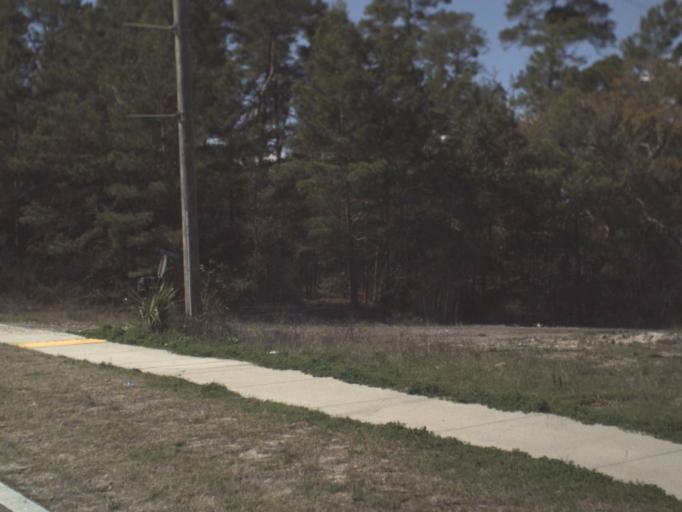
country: US
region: Florida
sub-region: Franklin County
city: Carrabelle
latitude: 29.8501
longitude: -84.6564
